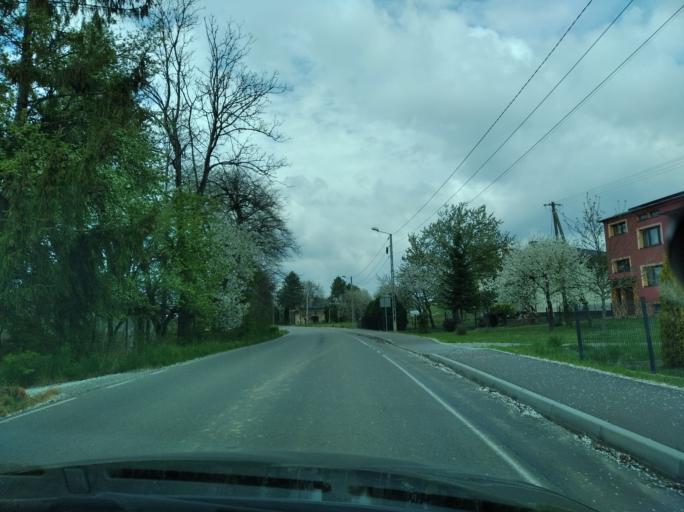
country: PL
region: Subcarpathian Voivodeship
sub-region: Powiat brzozowski
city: Haczow
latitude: 49.6561
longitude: 21.9098
